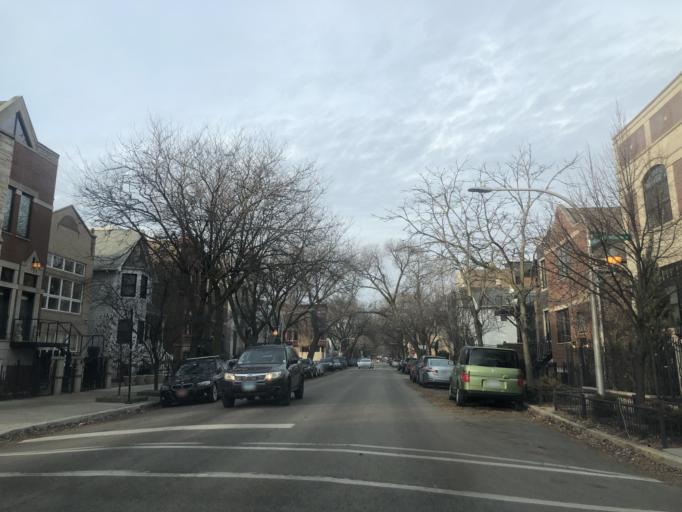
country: US
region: Illinois
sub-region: Cook County
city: Chicago
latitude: 41.9125
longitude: -87.6713
